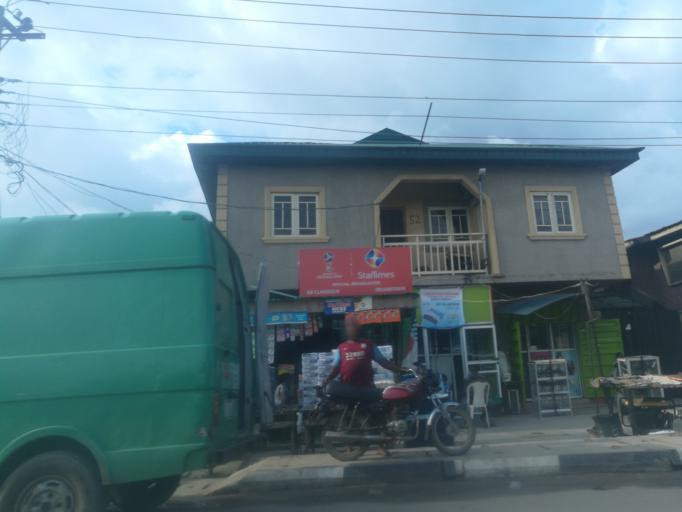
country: NG
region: Lagos
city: Somolu
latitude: 6.5391
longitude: 3.3833
